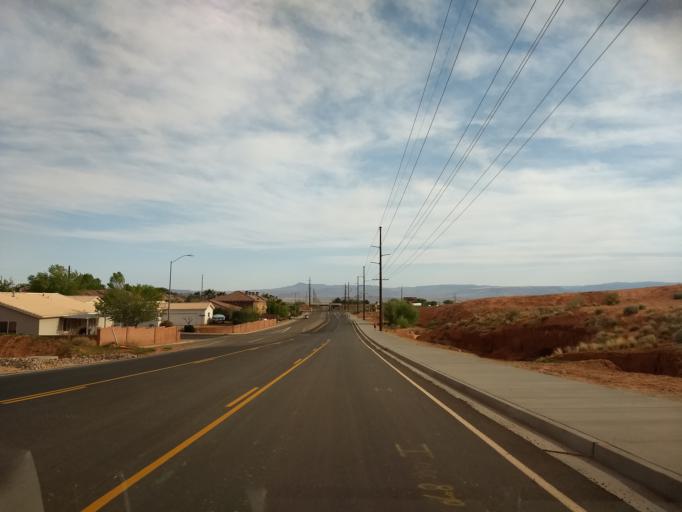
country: US
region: Utah
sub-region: Washington County
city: Washington
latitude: 37.1432
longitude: -113.5098
